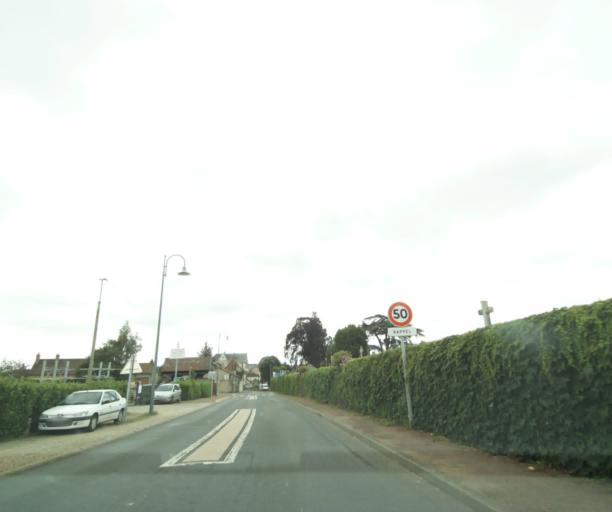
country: FR
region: Pays de la Loire
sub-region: Departement de la Sarthe
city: Precigne
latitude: 47.7696
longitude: -0.3230
